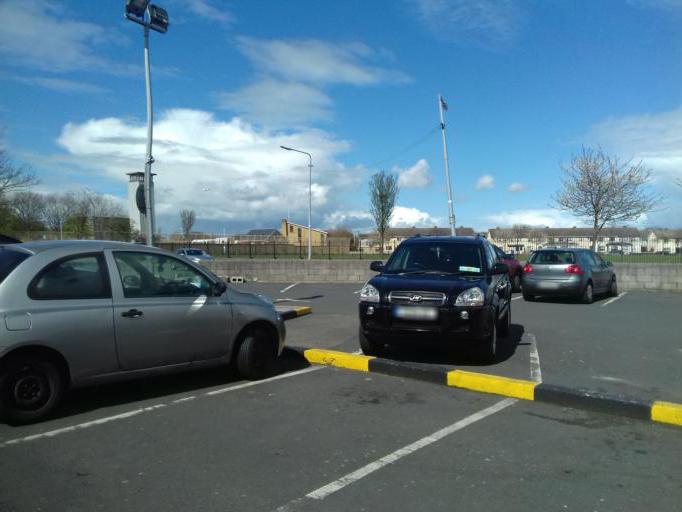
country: IE
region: Leinster
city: Donaghmede
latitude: 53.3890
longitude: -6.1678
